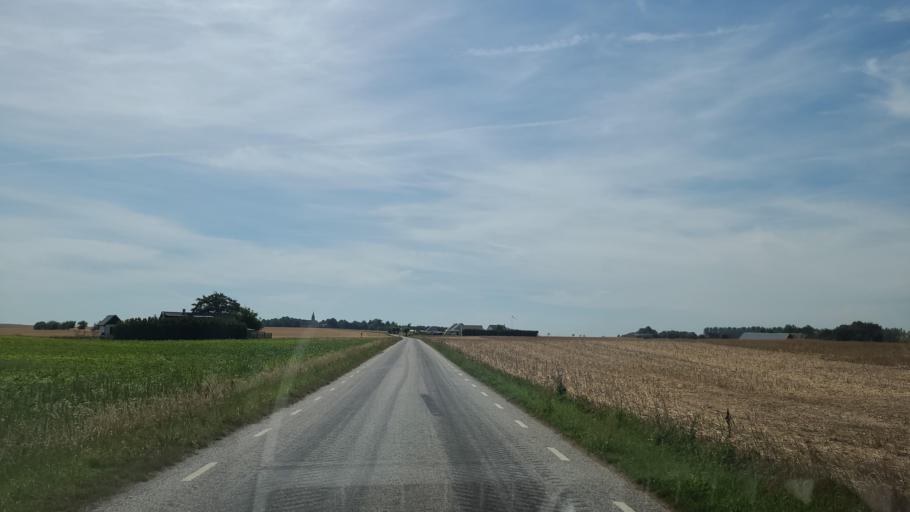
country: SE
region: Skane
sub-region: Malmo
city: Oxie
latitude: 55.4595
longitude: 13.0940
